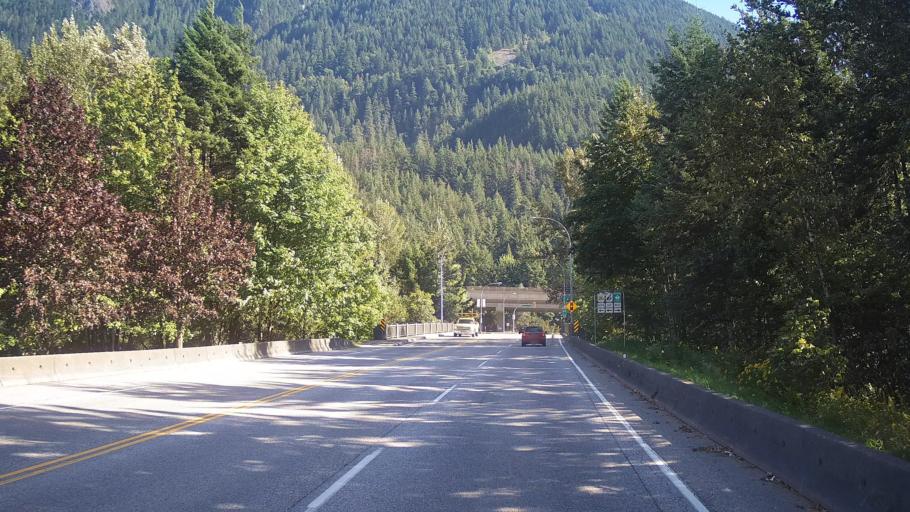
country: CA
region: British Columbia
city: Hope
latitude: 49.3752
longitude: -121.4421
